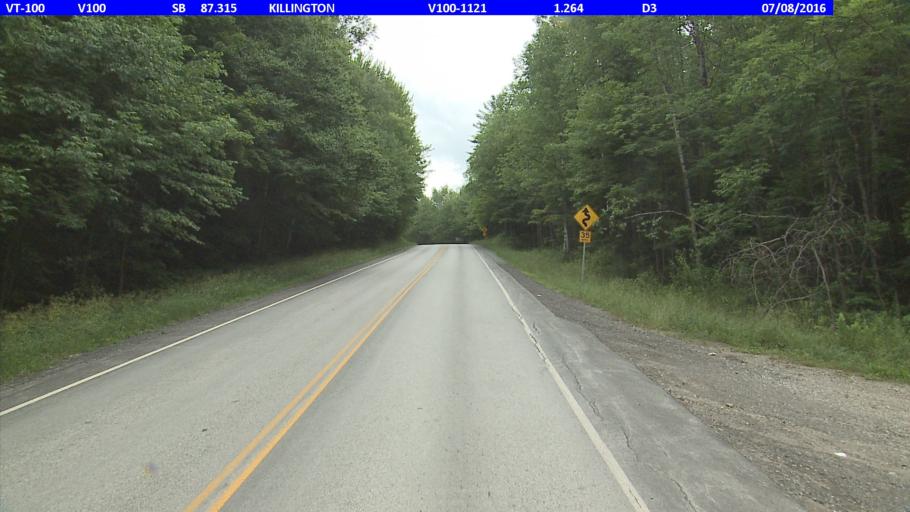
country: US
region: Vermont
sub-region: Rutland County
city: Rutland
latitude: 43.6842
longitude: -72.8136
